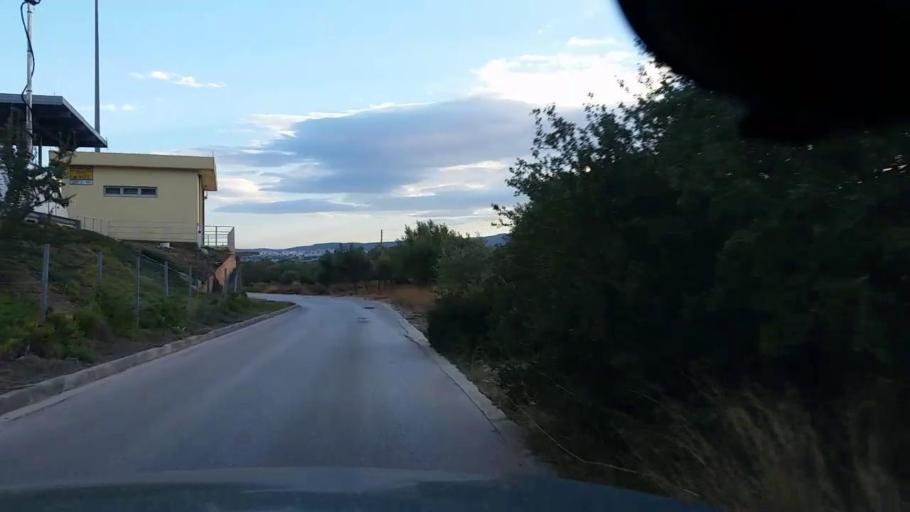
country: GR
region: Attica
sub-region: Nomarchia Anatolikis Attikis
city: Argithea
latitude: 37.9538
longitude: 23.8855
